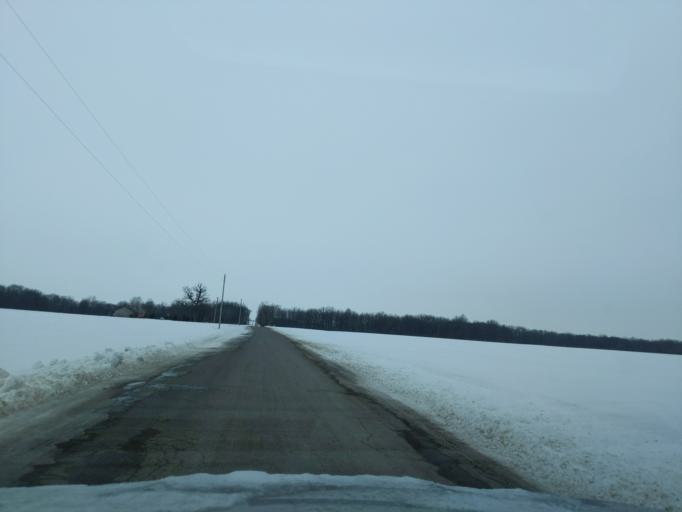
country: US
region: Indiana
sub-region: Benton County
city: Otterbein
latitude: 40.4152
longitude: -87.0915
